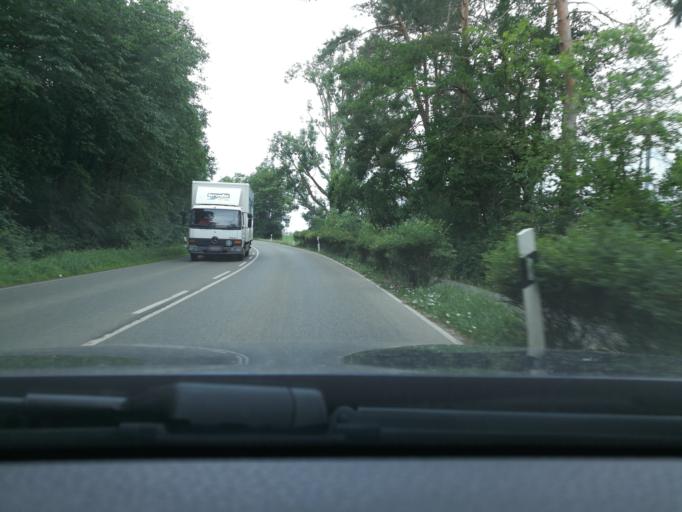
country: DE
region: Bavaria
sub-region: Regierungsbezirk Mittelfranken
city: Seukendorf
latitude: 49.4884
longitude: 10.9017
